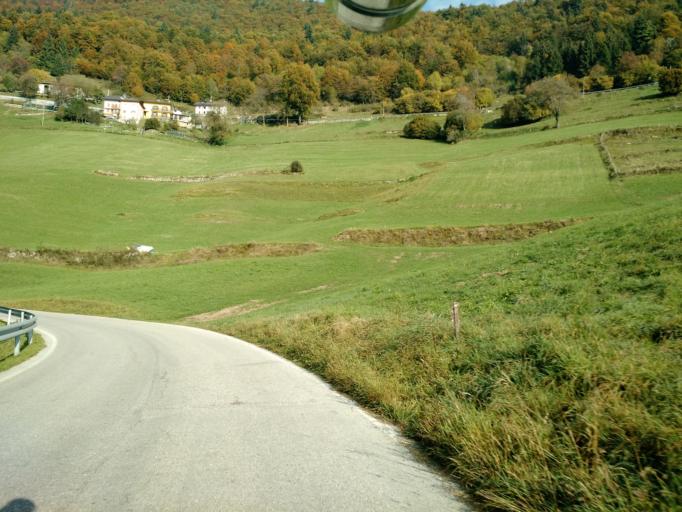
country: IT
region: Veneto
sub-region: Provincia di Vicenza
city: Foza
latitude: 45.8924
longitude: 11.5988
